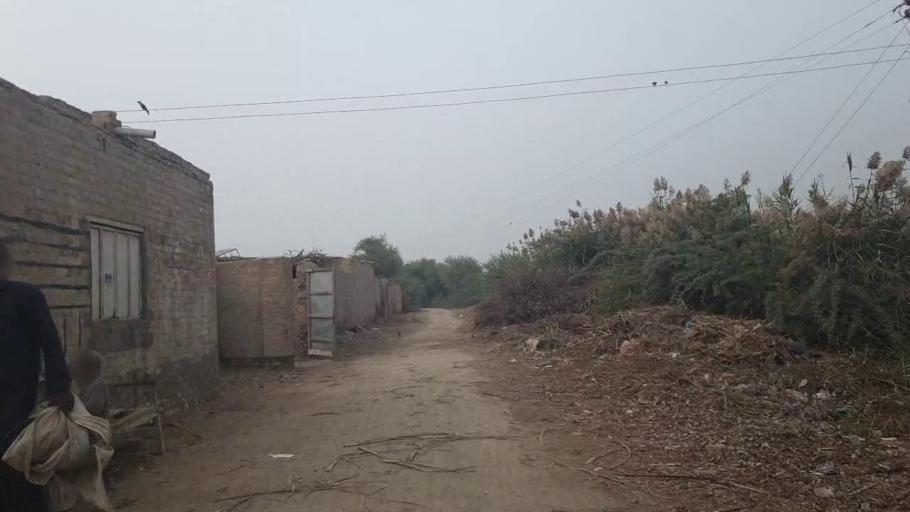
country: PK
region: Sindh
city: Tando Adam
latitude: 25.8129
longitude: 68.7173
